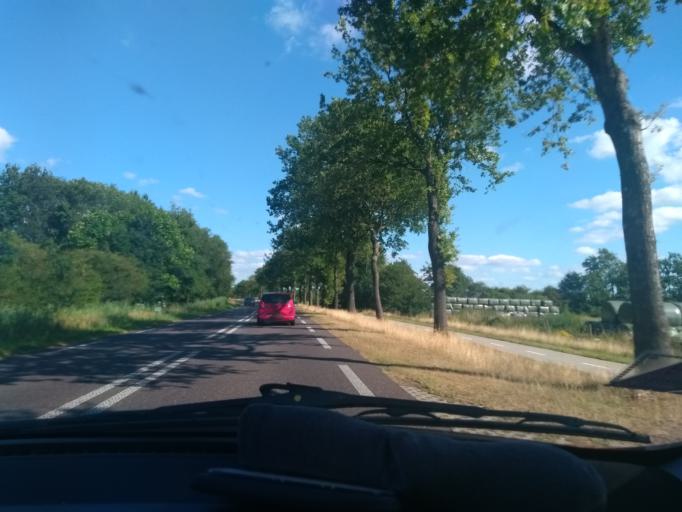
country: NL
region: Drenthe
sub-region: Gemeente Tynaarlo
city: Vries
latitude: 53.1088
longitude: 6.5221
